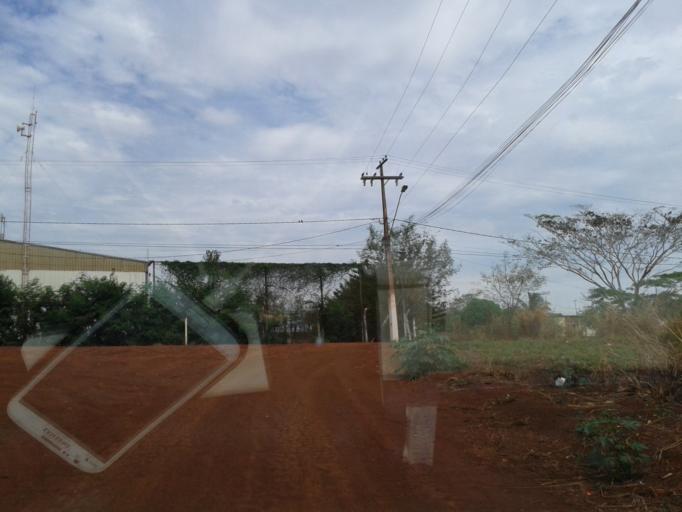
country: BR
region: Goias
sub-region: Itumbiara
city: Itumbiara
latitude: -18.4264
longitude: -49.1907
